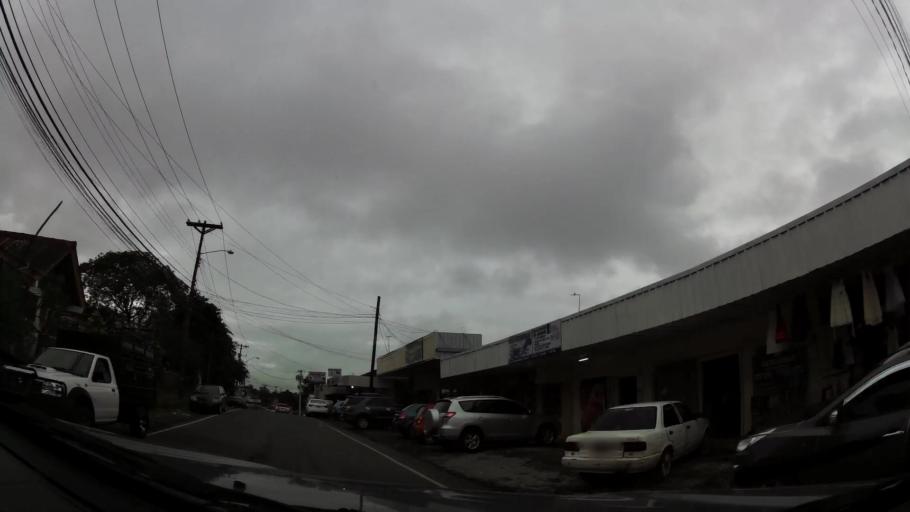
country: PA
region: Chiriqui
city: La Concepcion
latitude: 8.5161
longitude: -82.6201
